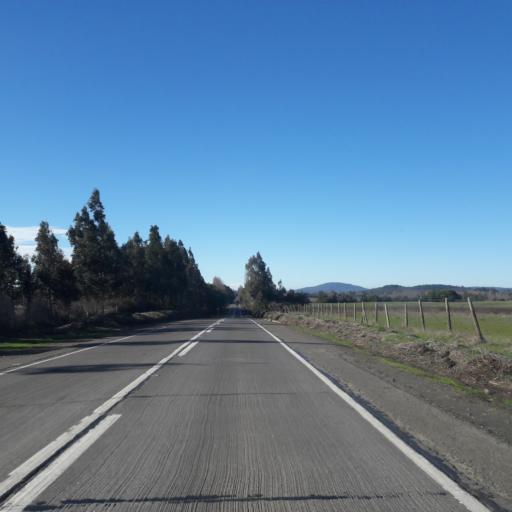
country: CL
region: Araucania
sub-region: Provincia de Malleco
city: Angol
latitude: -37.7538
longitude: -72.5824
